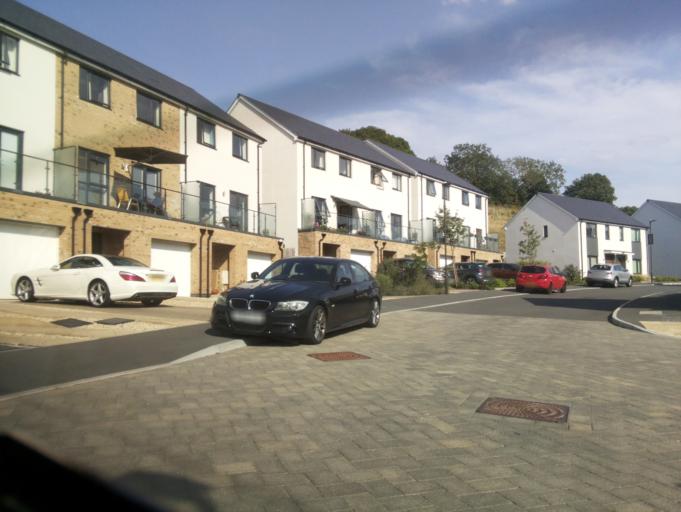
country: GB
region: England
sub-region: Gloucestershire
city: Dursley
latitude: 51.6871
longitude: -2.3508
